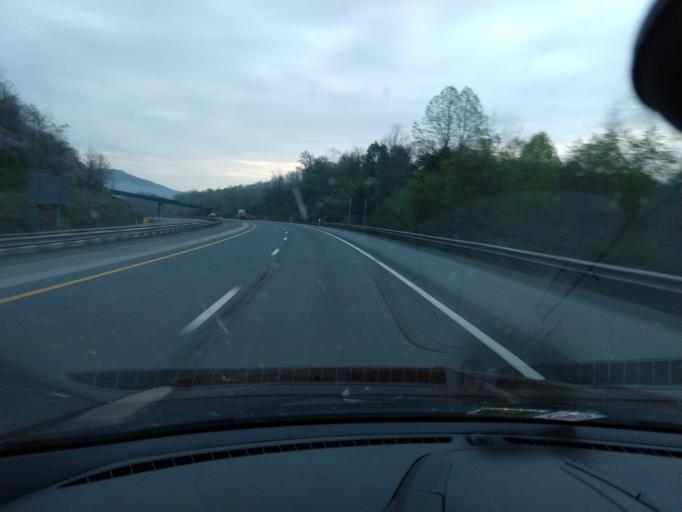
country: US
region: West Virginia
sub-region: Braxton County
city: Sutton
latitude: 38.6724
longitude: -80.7210
